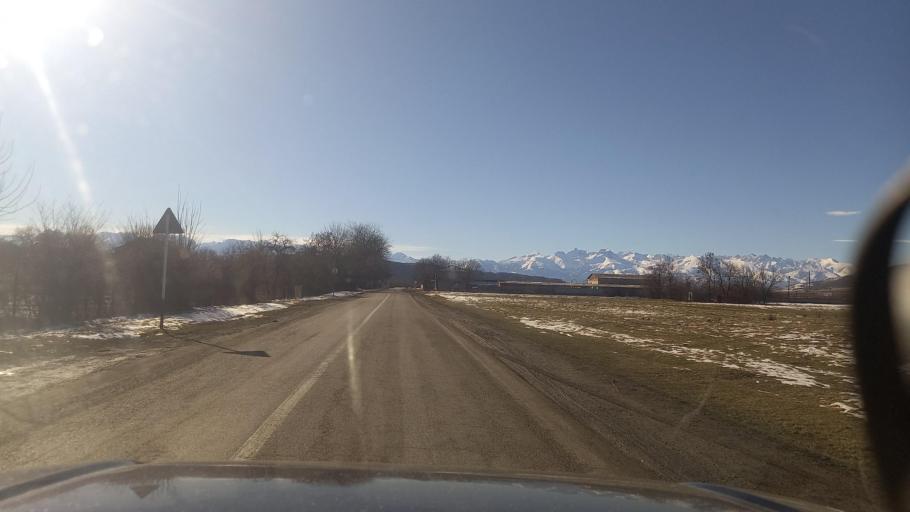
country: RU
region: Kabardino-Balkariya
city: Urukh
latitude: 43.2664
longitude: 43.9876
